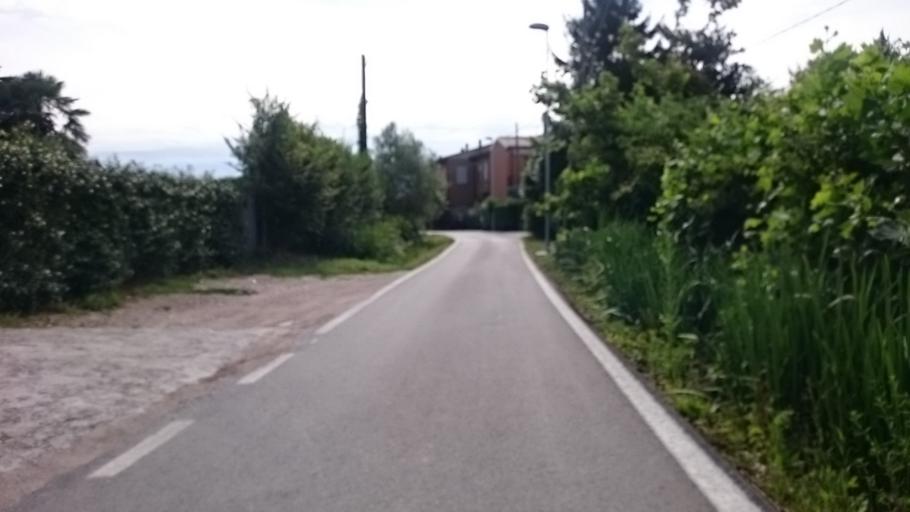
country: IT
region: Veneto
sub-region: Provincia di Padova
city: Albignasego
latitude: 45.3458
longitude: 11.8940
